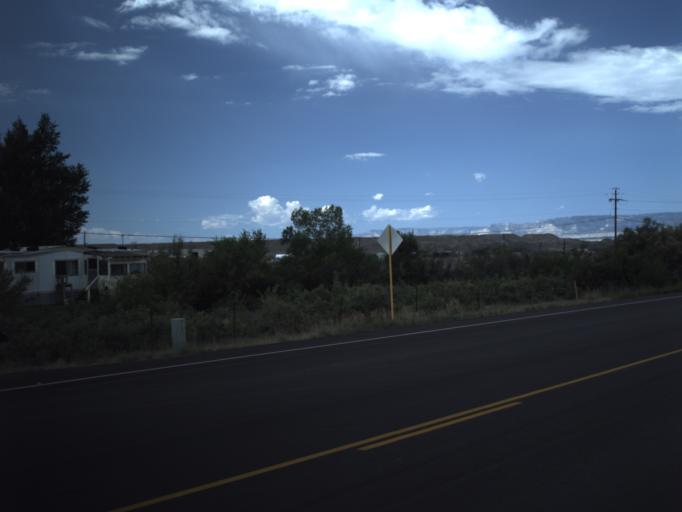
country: US
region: Utah
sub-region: Carbon County
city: Wellington
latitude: 39.5427
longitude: -110.6906
